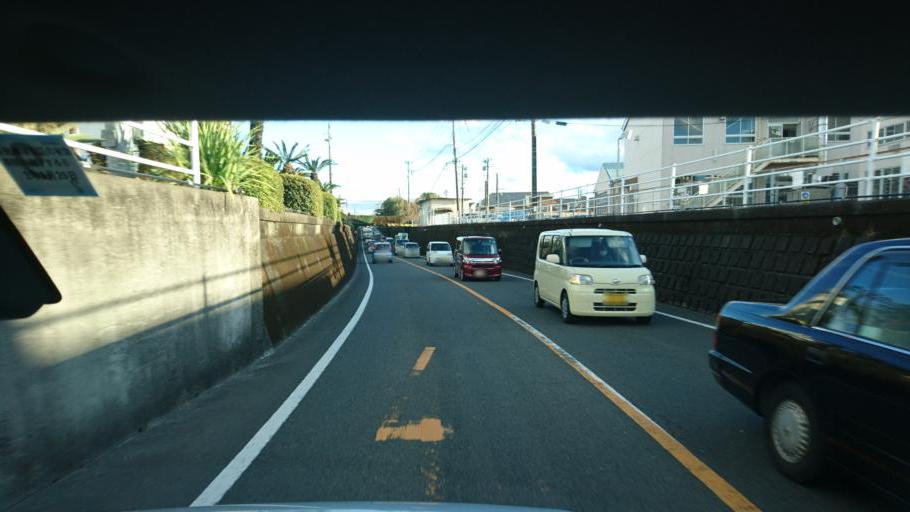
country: JP
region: Miyazaki
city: Miyazaki-shi
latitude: 31.8930
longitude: 131.4194
